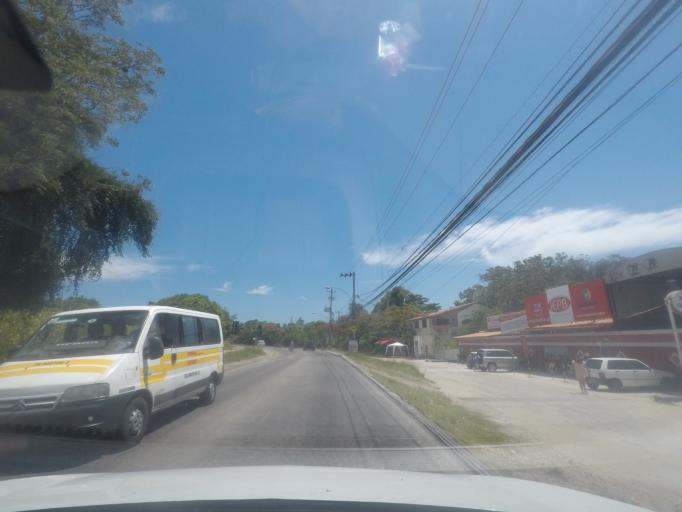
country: BR
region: Rio de Janeiro
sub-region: Itaguai
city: Itaguai
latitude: -22.9965
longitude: -43.6502
